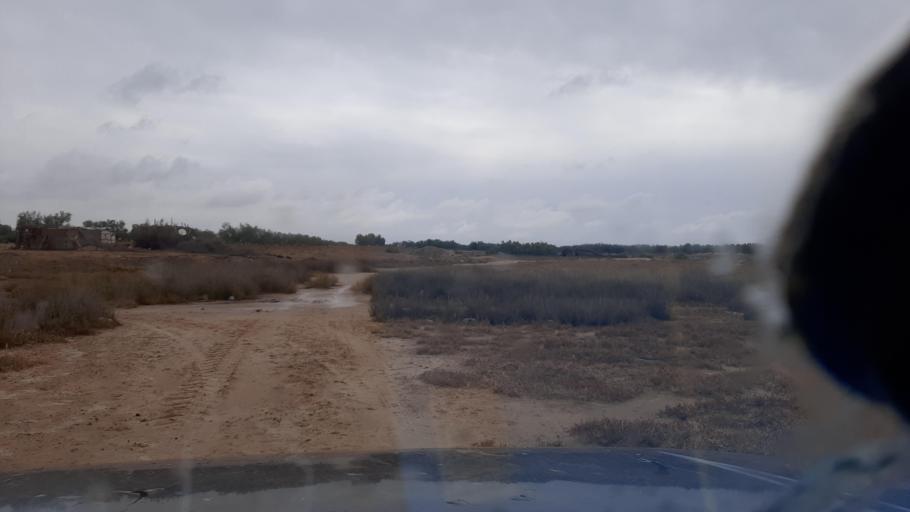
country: TN
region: Al Mahdiyah
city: Shurban
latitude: 35.4355
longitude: 10.4049
